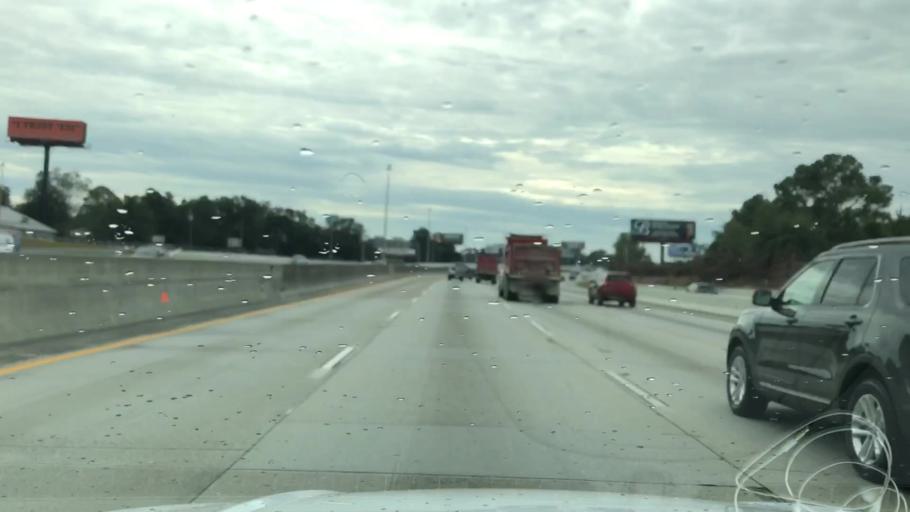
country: US
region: South Carolina
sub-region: Berkeley County
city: Hanahan
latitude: 32.8976
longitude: -80.0201
